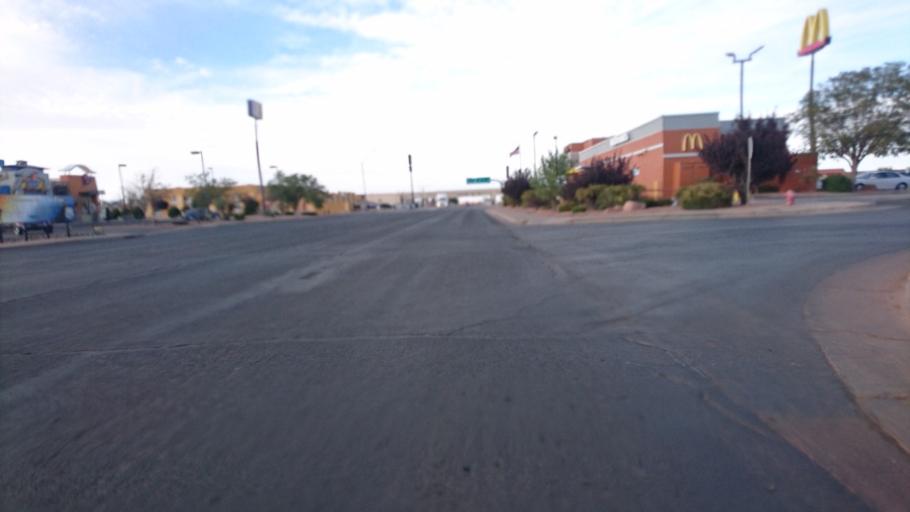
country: US
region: Arizona
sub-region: Navajo County
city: Winslow
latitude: 35.0365
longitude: -110.6978
